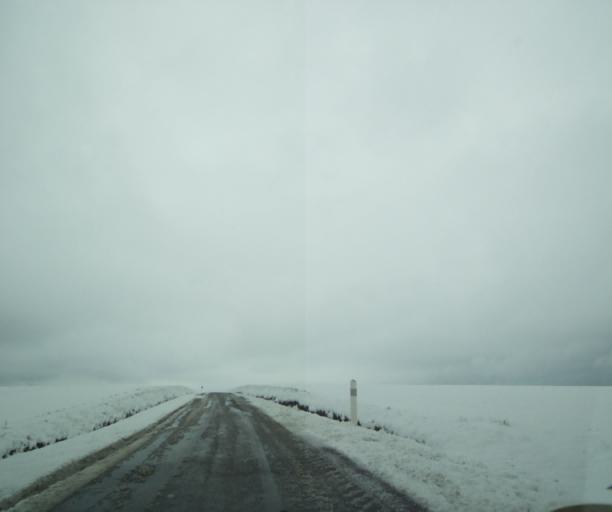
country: FR
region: Champagne-Ardenne
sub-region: Departement de la Haute-Marne
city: Laneuville-a-Remy
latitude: 48.3959
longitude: 4.8660
